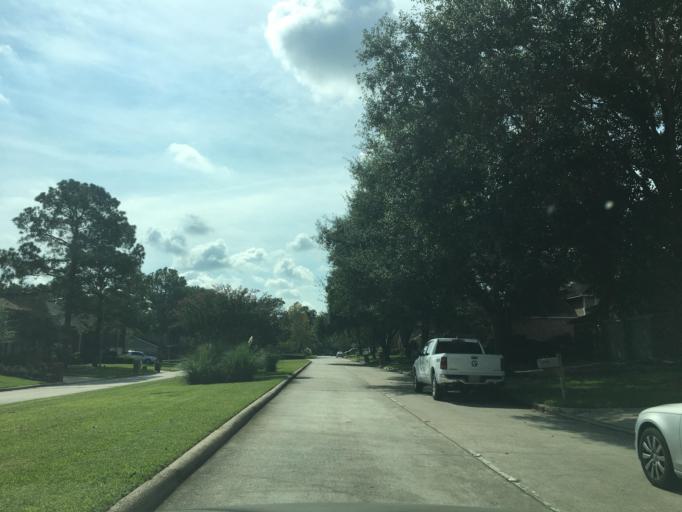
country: US
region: Texas
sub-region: Harris County
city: Spring
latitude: 30.0509
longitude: -95.4455
